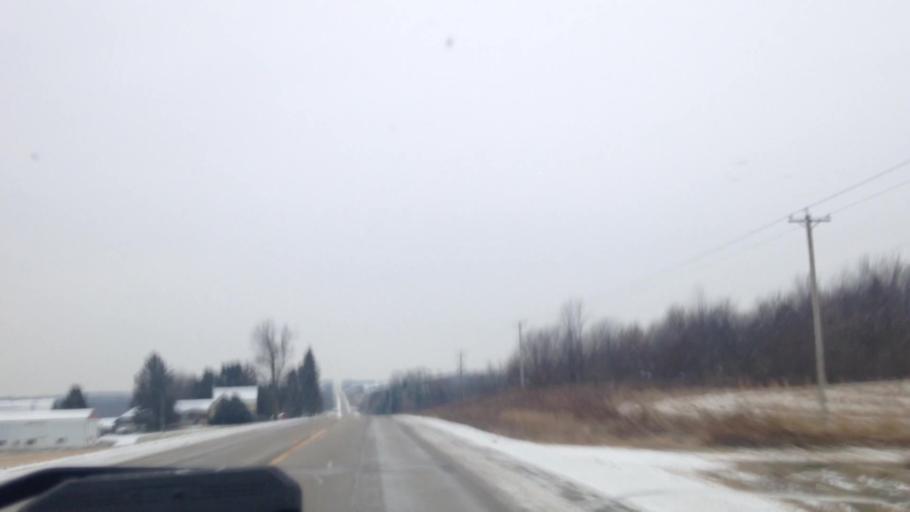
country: US
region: Wisconsin
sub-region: Dodge County
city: Hustisford
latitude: 43.2890
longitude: -88.5187
